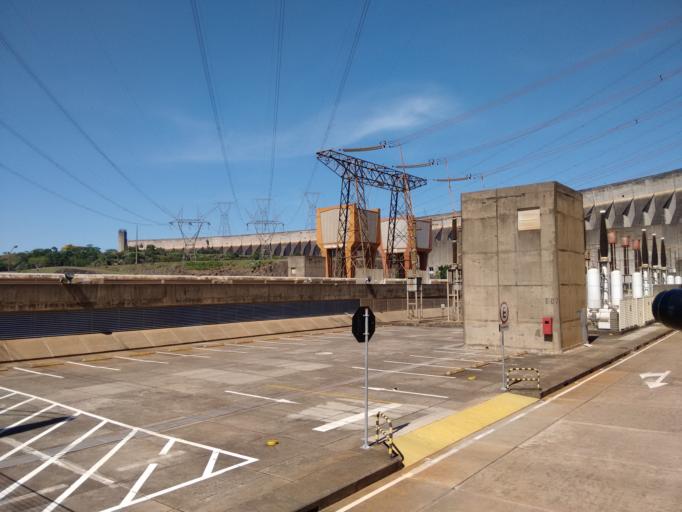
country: PY
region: Alto Parana
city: Ciudad del Este
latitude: -25.4075
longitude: -54.5911
